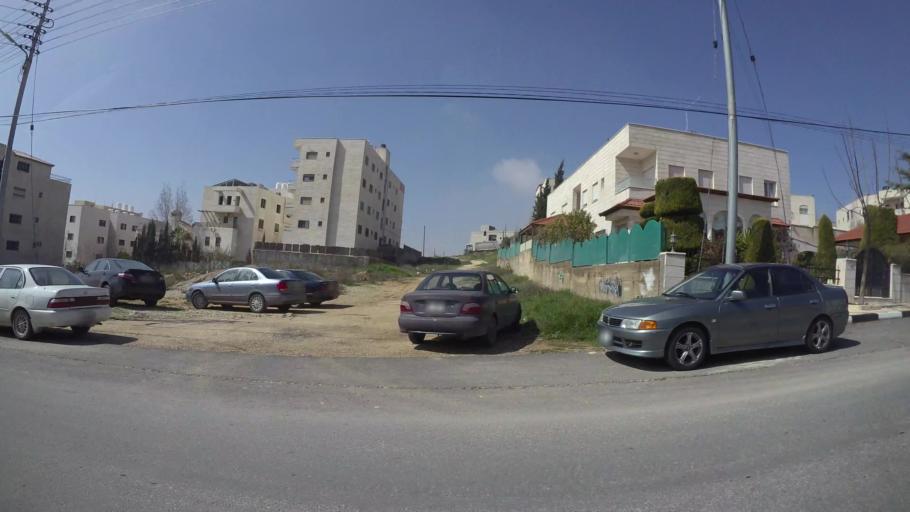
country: JO
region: Amman
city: Al Bunayyat ash Shamaliyah
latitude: 31.8977
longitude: 35.8764
